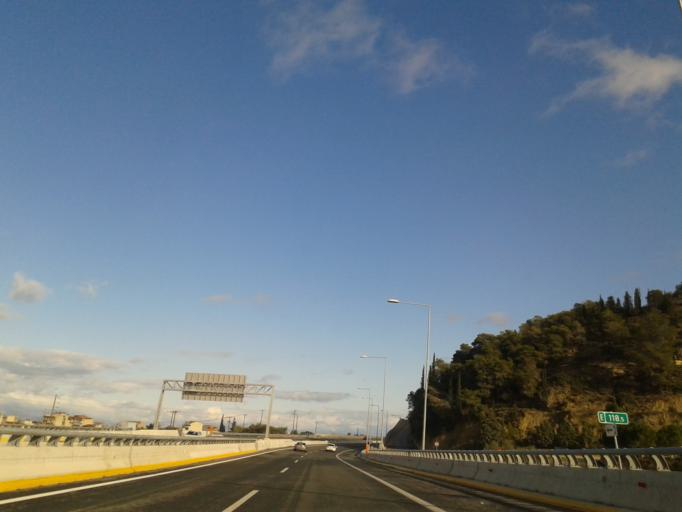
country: GR
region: Peloponnese
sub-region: Nomos Korinthias
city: Xylokastro
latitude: 38.0726
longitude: 22.6241
